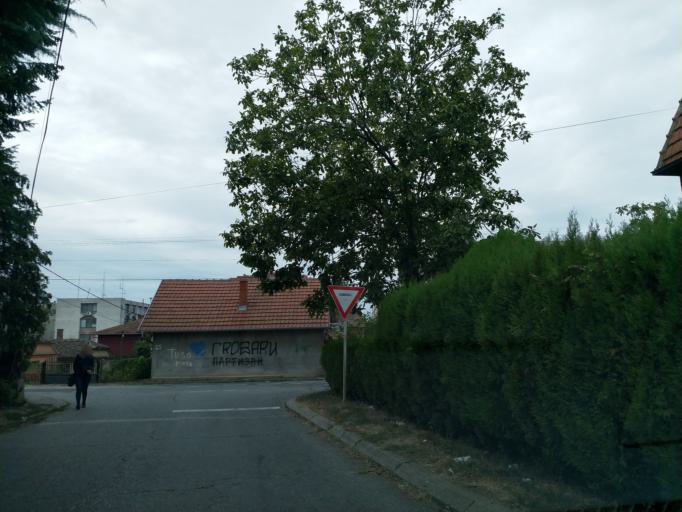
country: RS
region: Central Serbia
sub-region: Pomoravski Okrug
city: Paracin
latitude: 43.8655
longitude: 21.4104
